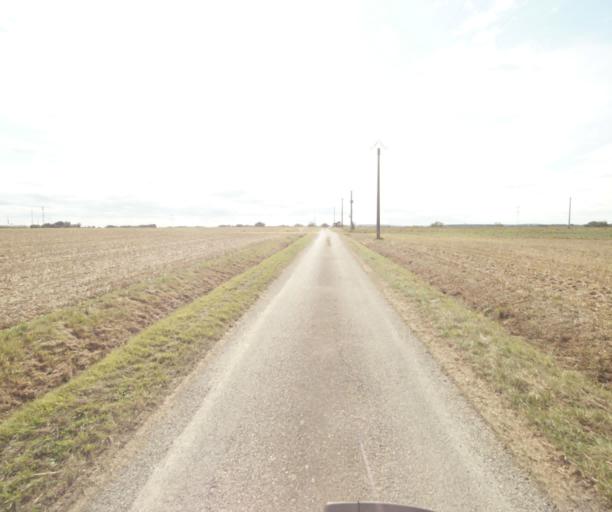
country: FR
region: Midi-Pyrenees
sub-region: Departement du Tarn-et-Garonne
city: Finhan
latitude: 43.8750
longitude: 1.1868
